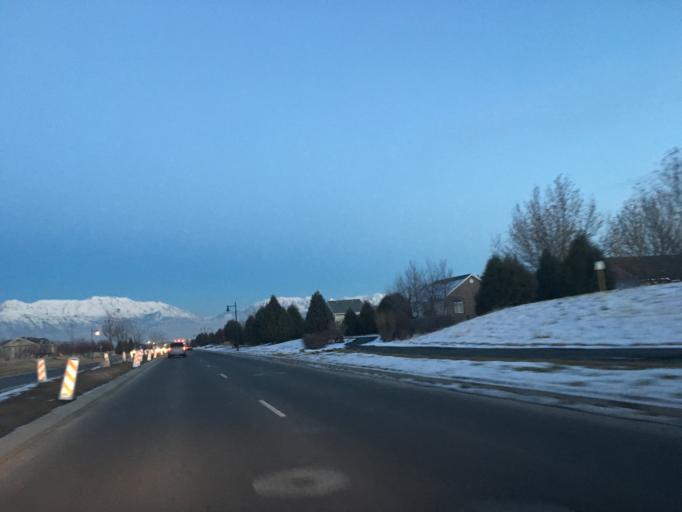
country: US
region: Utah
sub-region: Utah County
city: Eagle Mountain
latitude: 40.3621
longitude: -111.9828
